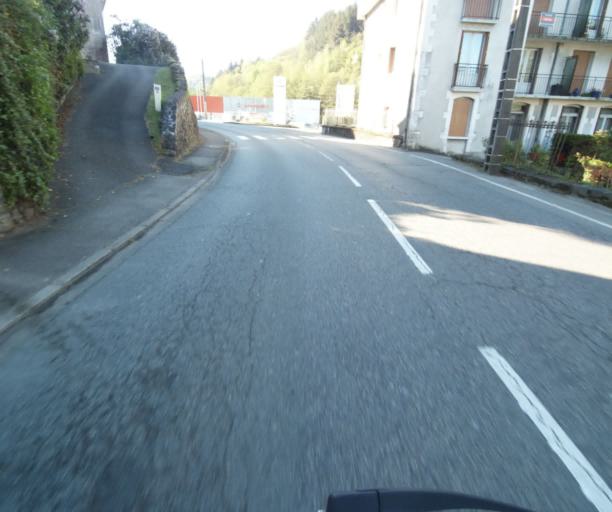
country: FR
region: Limousin
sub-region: Departement de la Correze
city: Laguenne
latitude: 45.2501
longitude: 1.7663
